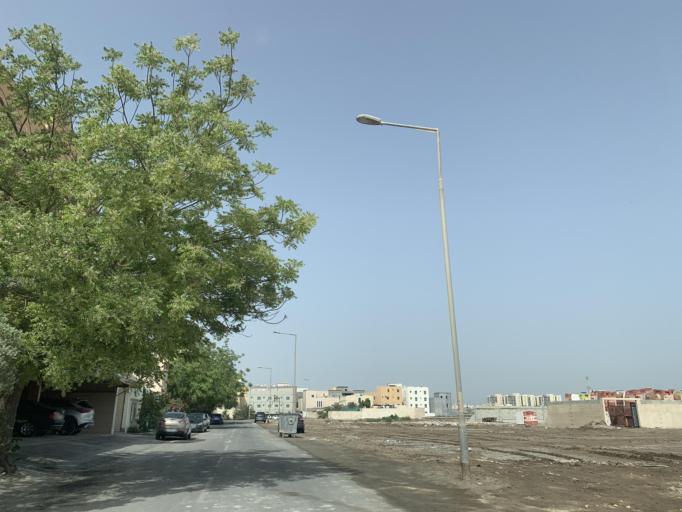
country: BH
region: Northern
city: Sitrah
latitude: 26.1313
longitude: 50.5957
